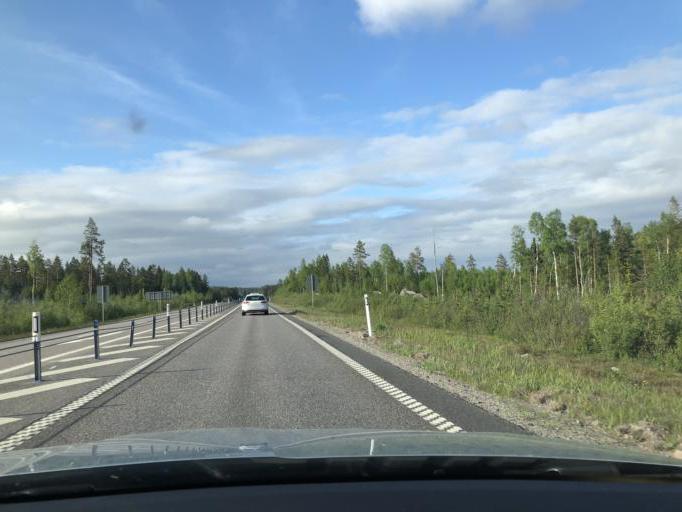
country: SE
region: Vaesternorrland
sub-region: Sundsvalls Kommun
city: Njurundabommen
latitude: 62.0965
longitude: 17.3072
